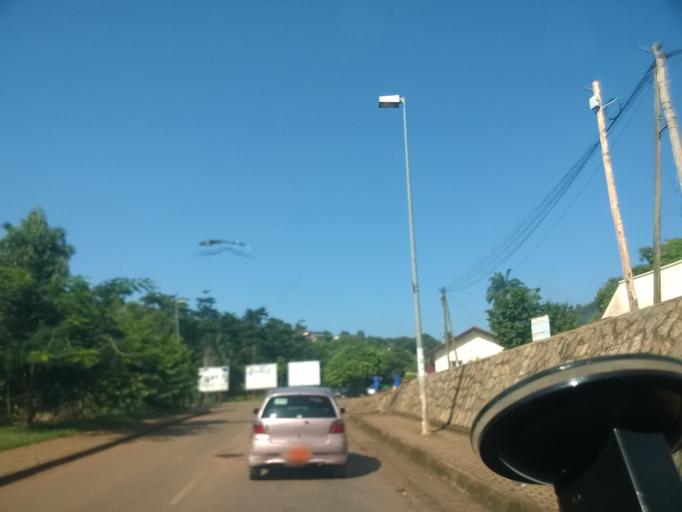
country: CM
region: Centre
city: Yaounde
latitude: 3.8596
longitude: 11.5106
